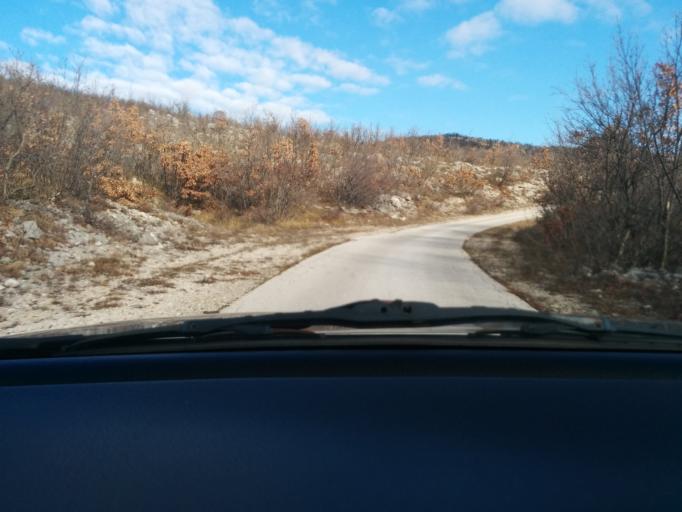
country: HR
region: Splitsko-Dalmatinska
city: Hrvace
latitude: 43.8026
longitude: 16.6843
